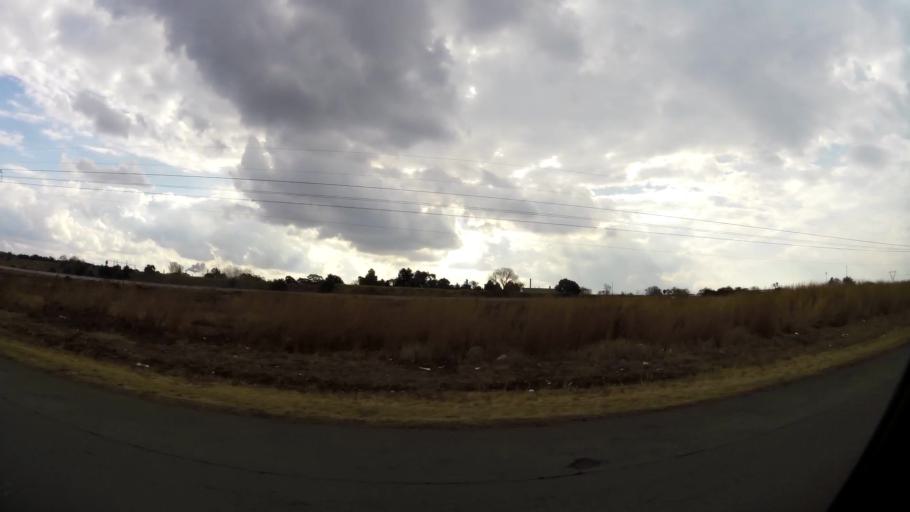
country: ZA
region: Gauteng
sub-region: Sedibeng District Municipality
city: Vanderbijlpark
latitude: -26.6636
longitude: 27.8427
